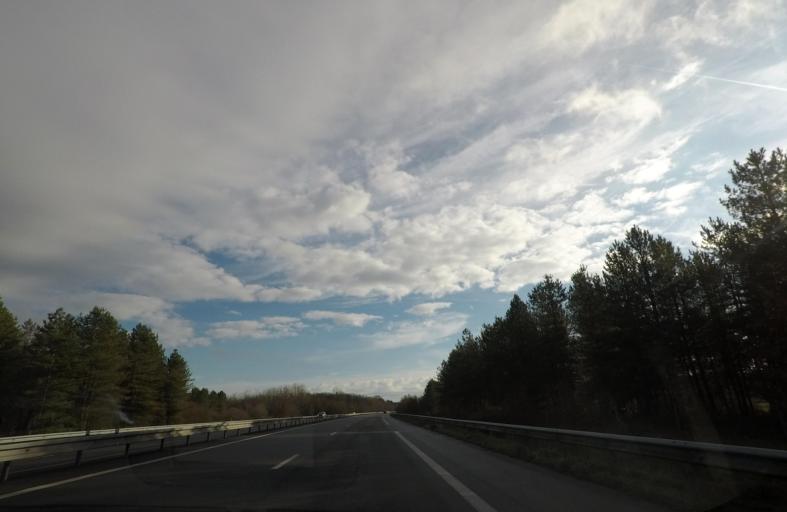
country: FR
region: Centre
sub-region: Departement du Loir-et-Cher
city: Chatres-sur-Cher
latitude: 47.3069
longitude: 1.8496
